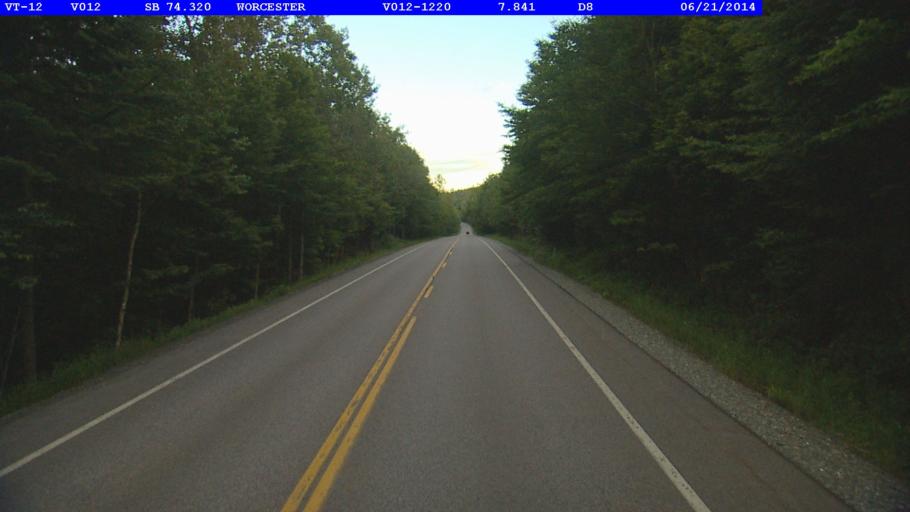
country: US
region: Vermont
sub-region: Lamoille County
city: Morrisville
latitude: 44.4519
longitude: -72.5464
